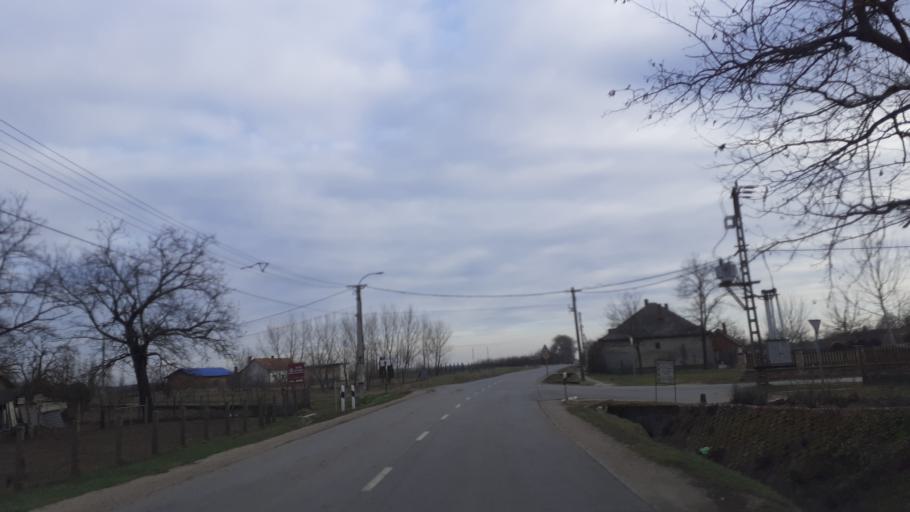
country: HU
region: Fejer
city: Sarkeresztur
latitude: 46.9999
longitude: 18.5550
